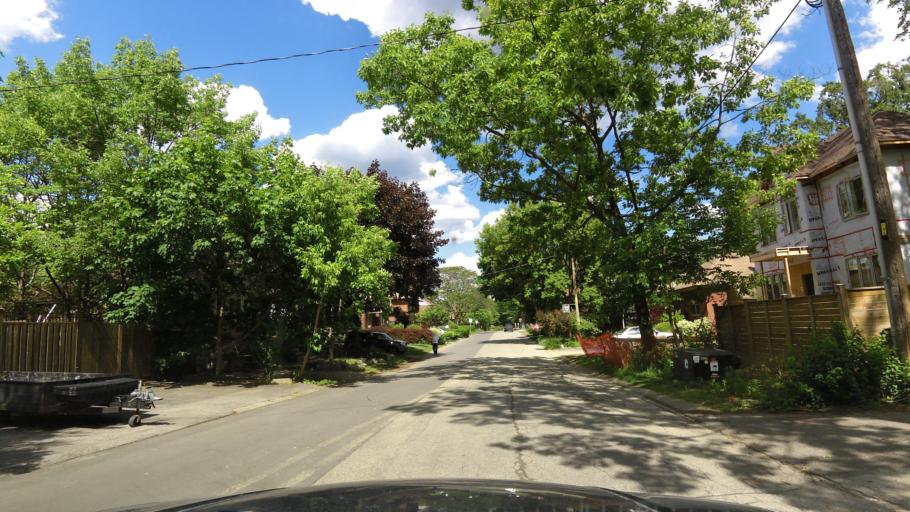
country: CA
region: Ontario
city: Etobicoke
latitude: 43.5902
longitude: -79.5336
